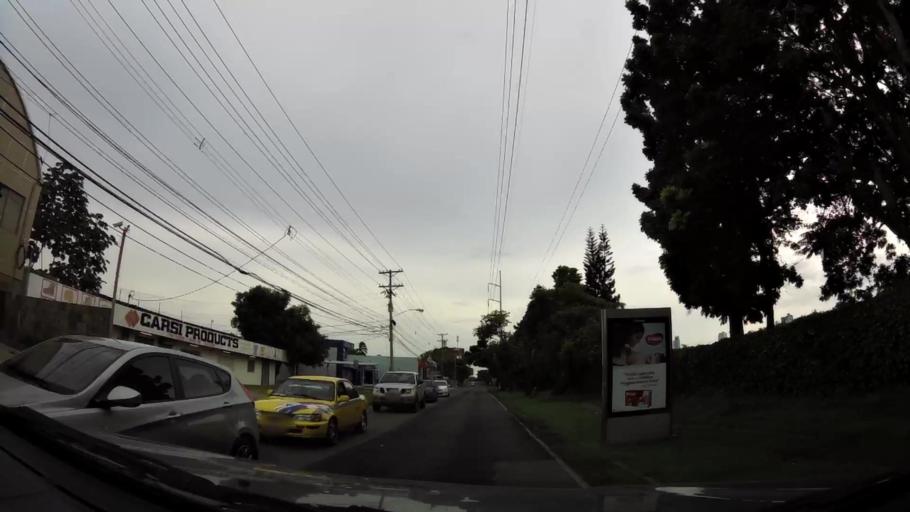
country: PA
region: Panama
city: Panama
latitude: 9.0115
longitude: -79.4942
